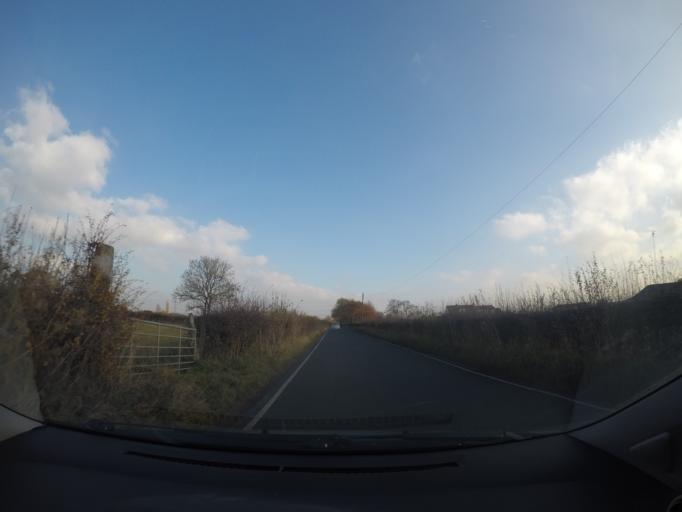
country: GB
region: England
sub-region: City of York
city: Huntington
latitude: 53.9987
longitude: -1.0490
